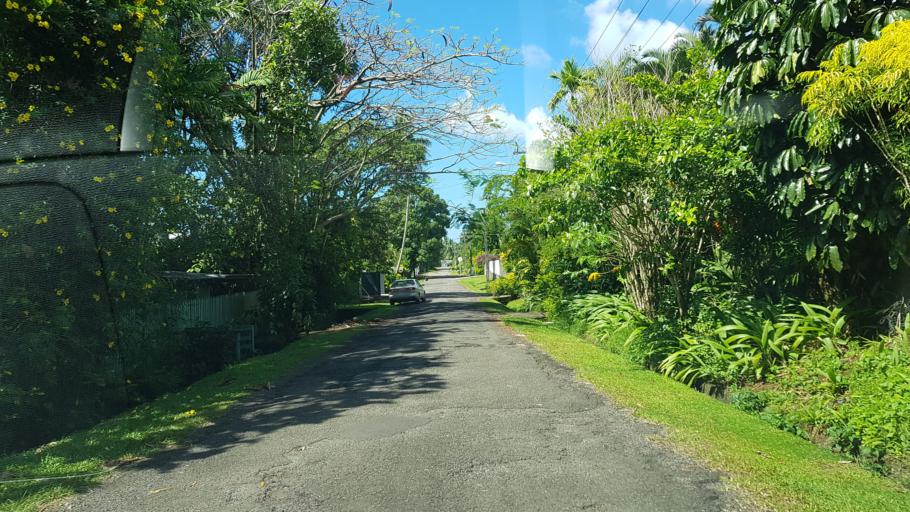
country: FJ
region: Central
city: Suva
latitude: -18.1456
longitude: 178.4558
